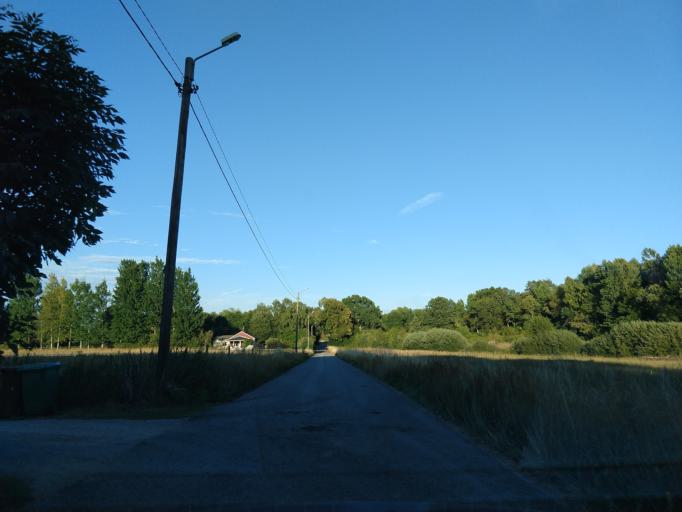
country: SE
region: Blekinge
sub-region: Ronneby Kommun
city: Brakne-Hoby
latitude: 56.2610
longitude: 15.1237
